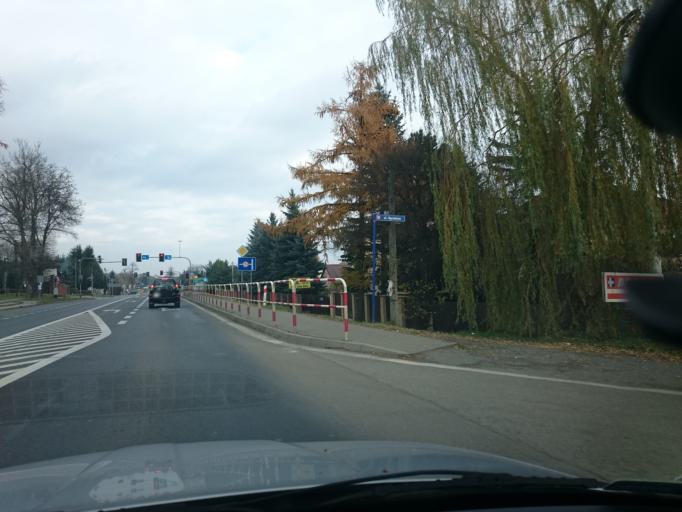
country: PL
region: Lesser Poland Voivodeship
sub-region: Powiat krakowski
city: Michalowice
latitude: 50.1579
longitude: 19.9807
